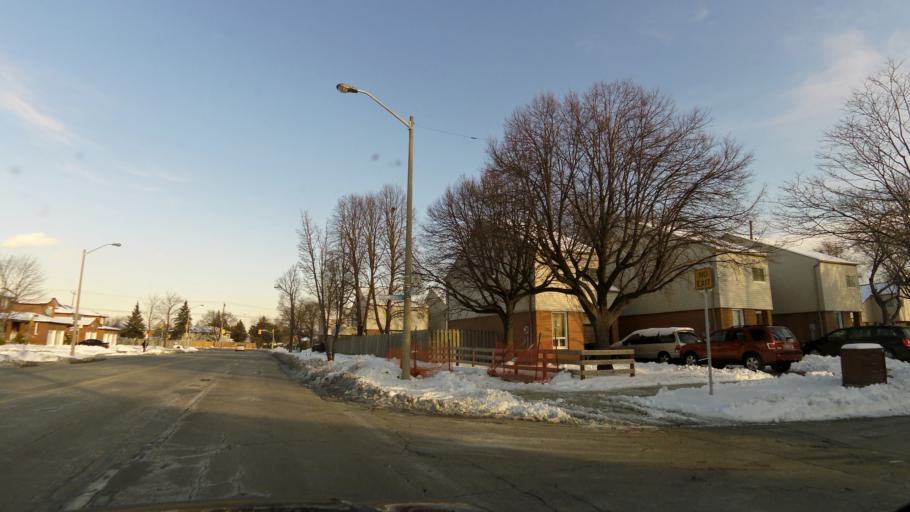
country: CA
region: Ontario
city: Etobicoke
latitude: 43.7351
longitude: -79.5799
